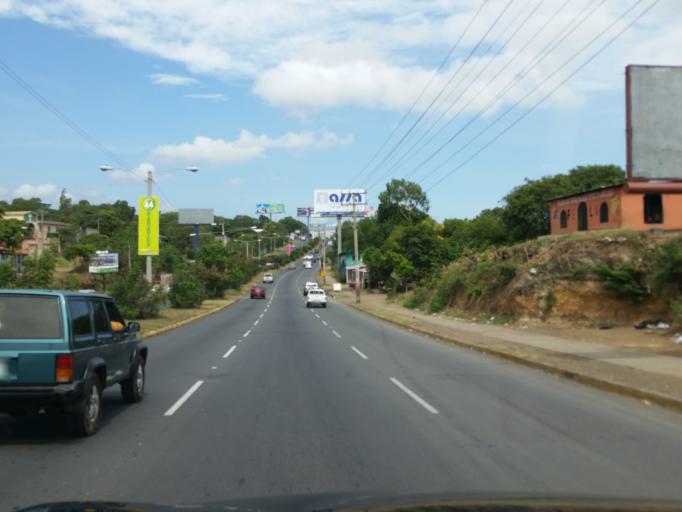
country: NI
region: Managua
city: Managua
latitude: 12.1091
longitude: -86.2830
